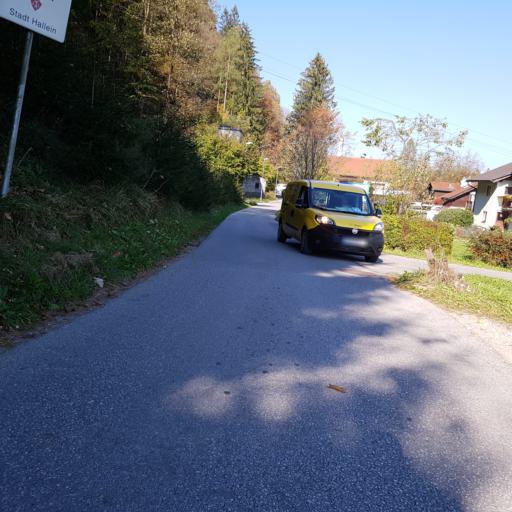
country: AT
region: Salzburg
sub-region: Politischer Bezirk Hallein
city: Hallein
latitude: 47.6677
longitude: 13.1086
